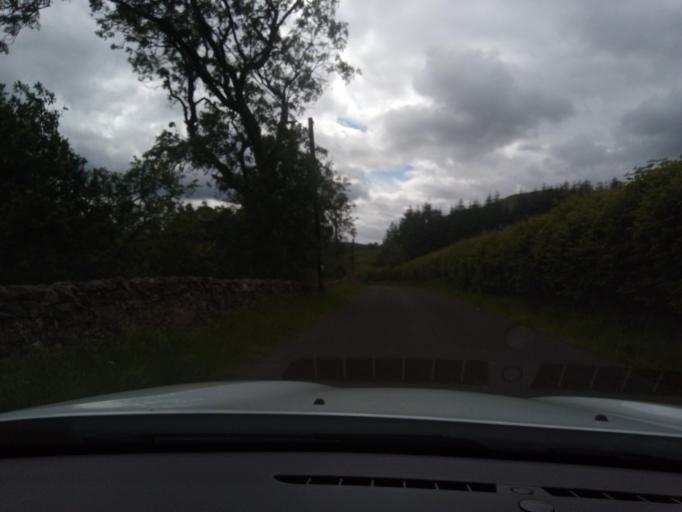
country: GB
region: Scotland
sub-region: The Scottish Borders
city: Innerleithen
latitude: 55.4513
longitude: -3.1025
